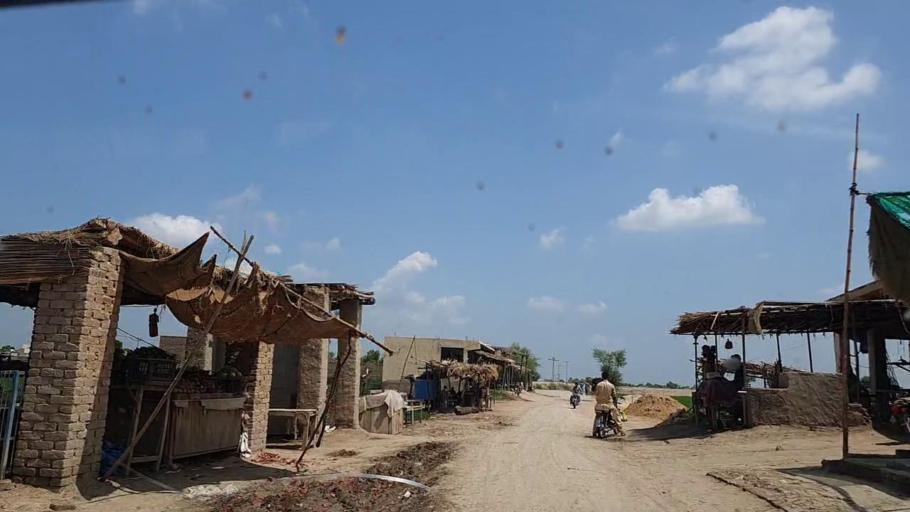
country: PK
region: Sindh
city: Tharu Shah
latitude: 26.9874
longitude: 68.0769
